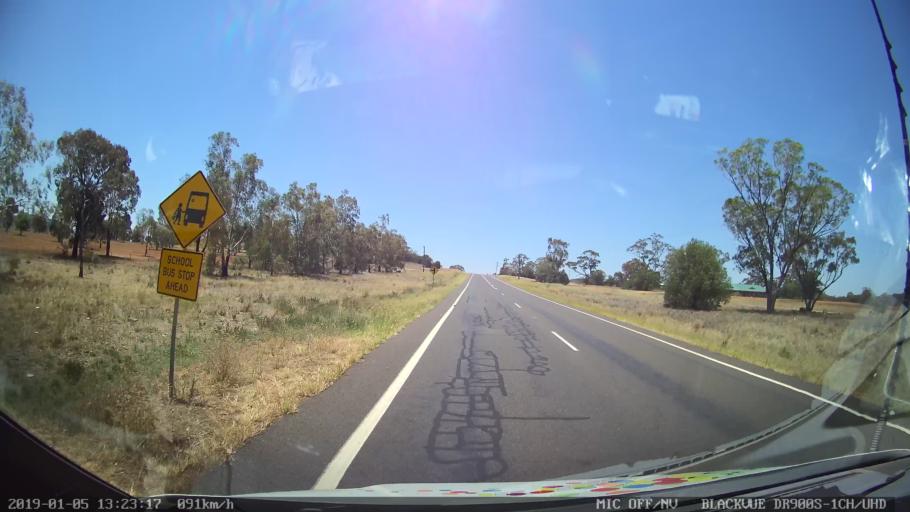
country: AU
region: New South Wales
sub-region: Gunnedah
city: Gunnedah
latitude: -31.0792
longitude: 149.9731
